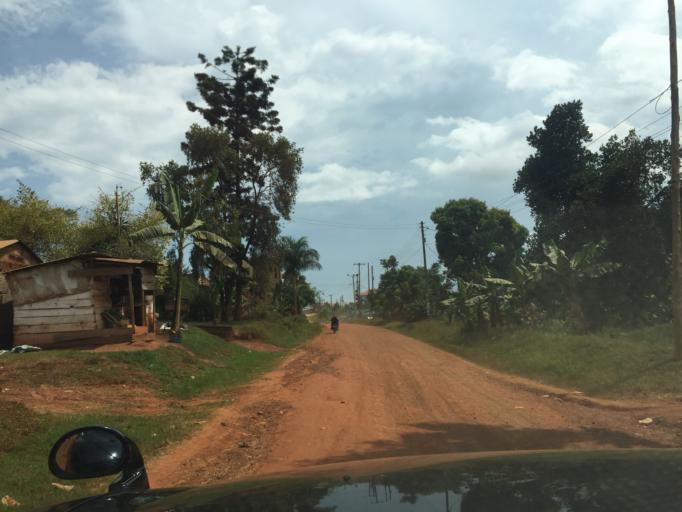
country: UG
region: Central Region
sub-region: Wakiso District
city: Kireka
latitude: 0.4103
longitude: 32.6203
